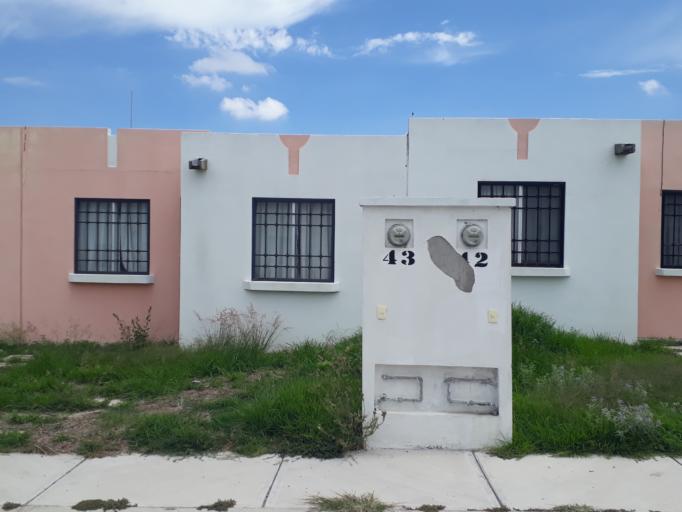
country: MX
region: Aguascalientes
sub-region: Aguascalientes
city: San Sebastian [Fraccionamiento]
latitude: 21.8051
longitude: -102.2683
